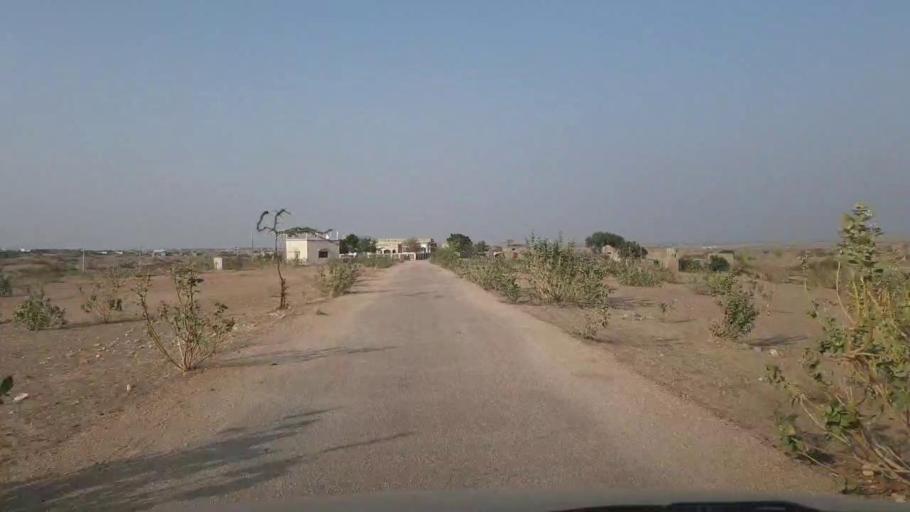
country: PK
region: Sindh
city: Umarkot
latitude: 25.3479
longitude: 69.7638
